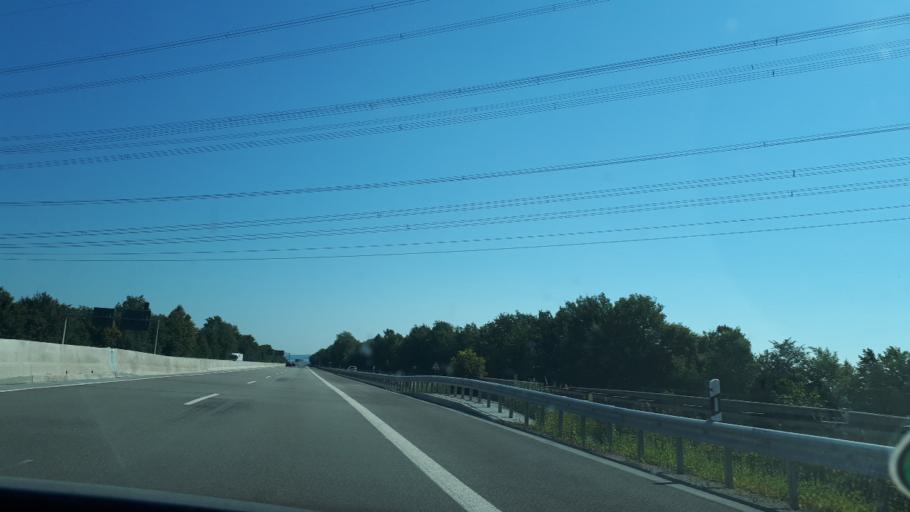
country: DE
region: Rheinland-Pfalz
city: Bassenheim
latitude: 50.3604
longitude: 7.4866
